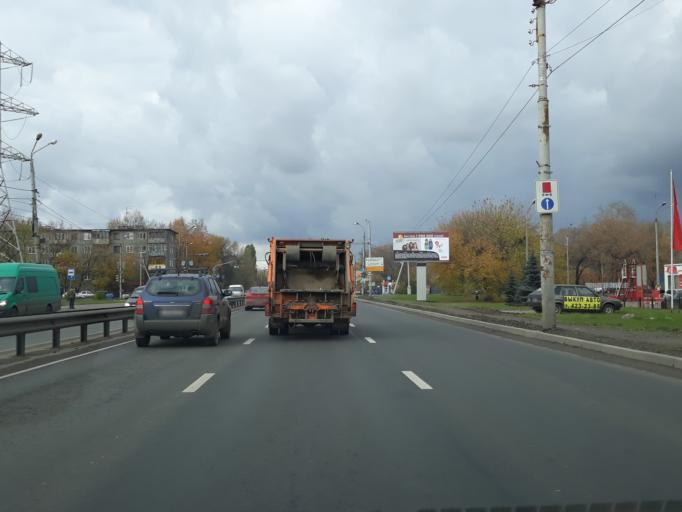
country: RU
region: Nizjnij Novgorod
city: Nizhniy Novgorod
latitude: 56.2577
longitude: 43.9339
